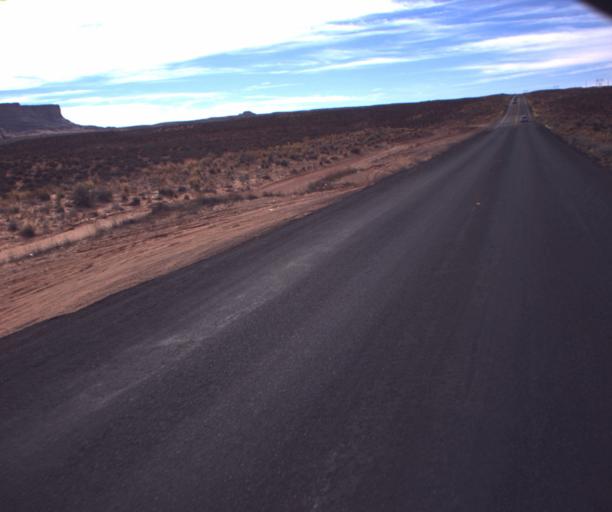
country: US
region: Arizona
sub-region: Coconino County
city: LeChee
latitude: 36.8739
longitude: -111.3427
